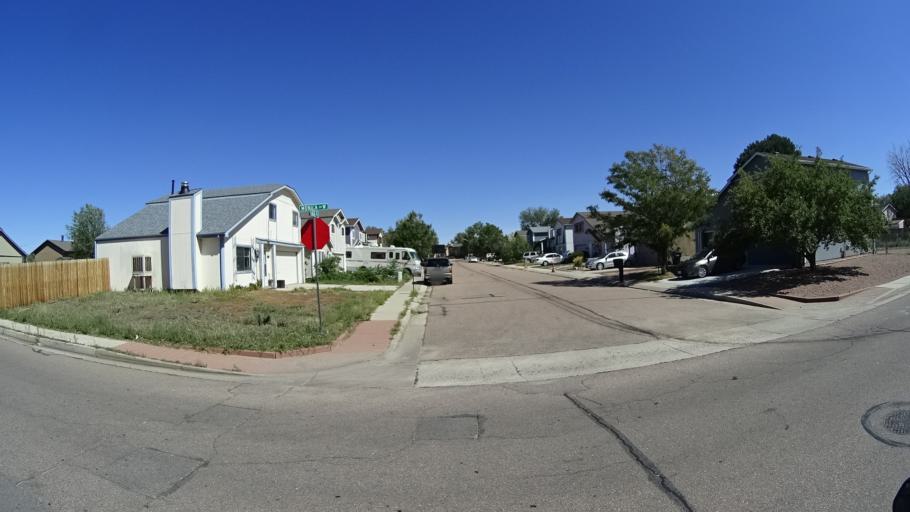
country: US
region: Colorado
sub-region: El Paso County
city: Stratmoor
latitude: 38.7871
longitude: -104.7471
